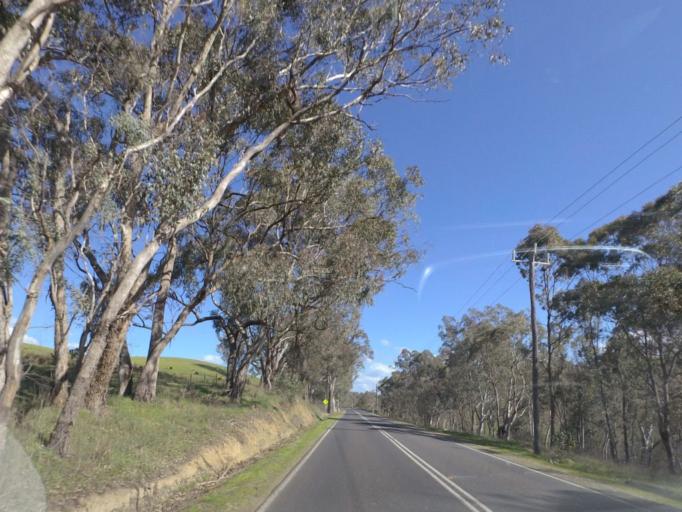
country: AU
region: Victoria
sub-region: Murrindindi
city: Alexandra
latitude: -37.2076
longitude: 145.7322
